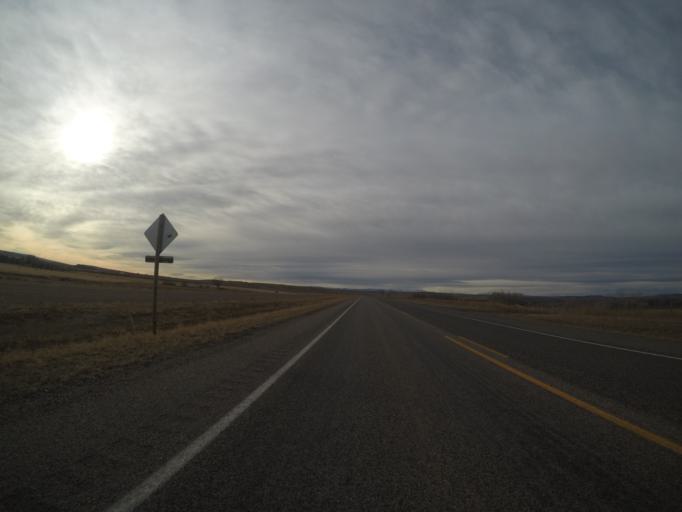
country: US
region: Montana
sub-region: Yellowstone County
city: Laurel
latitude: 45.6164
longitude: -108.8164
